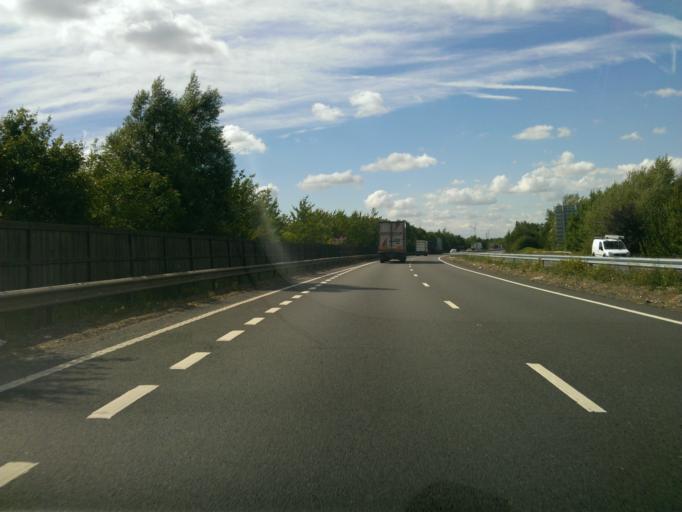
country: GB
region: England
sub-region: Cambridgeshire
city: Brampton
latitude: 52.3289
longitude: -0.2370
